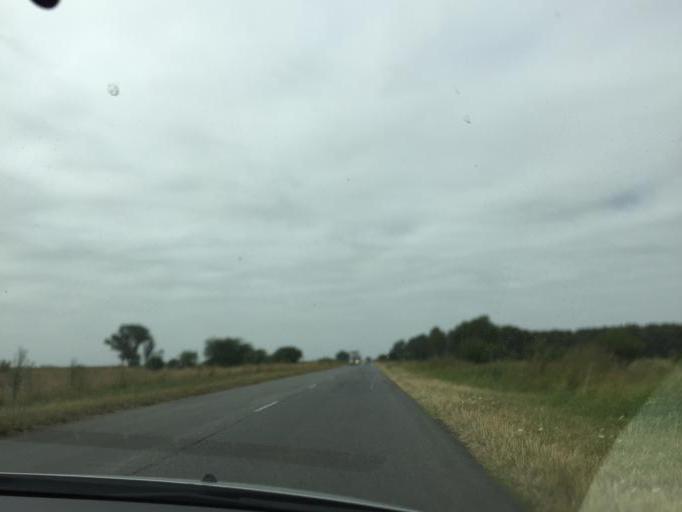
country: AR
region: Buenos Aires
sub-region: Partido de Las Flores
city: Las Flores
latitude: -36.2227
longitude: -59.0448
